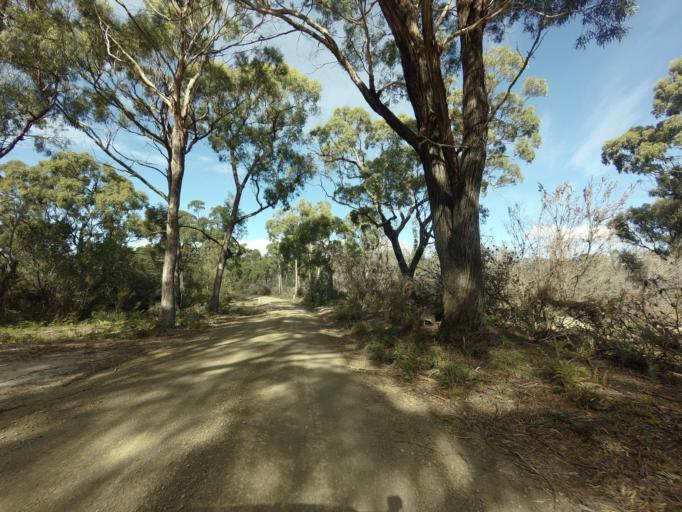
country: AU
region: Tasmania
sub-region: Clarence
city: Sandford
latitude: -42.9767
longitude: 147.7166
